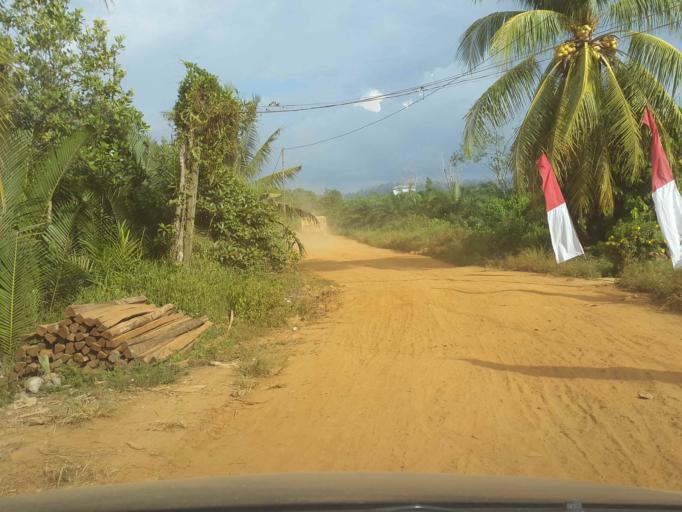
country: ID
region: West Kalimantan
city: Pemangkat
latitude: 1.7832
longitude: 109.3405
